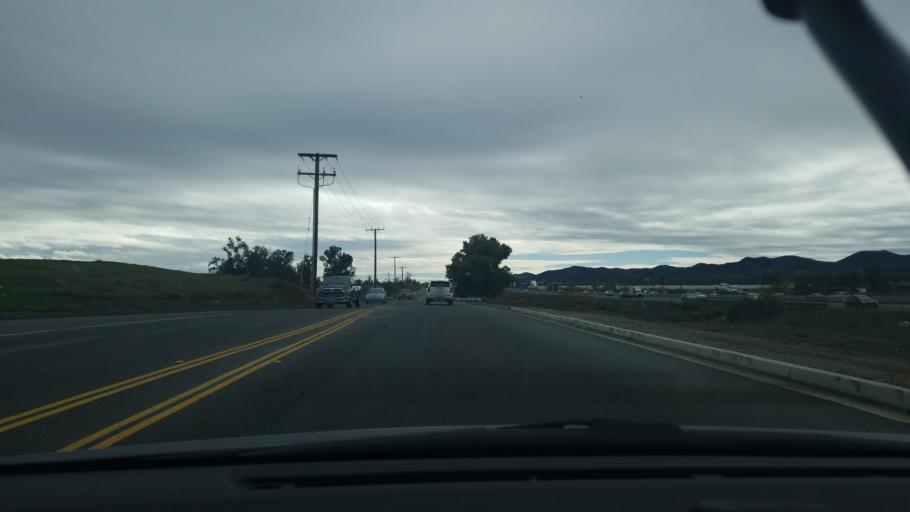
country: US
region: California
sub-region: Riverside County
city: Sun City
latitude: 33.6600
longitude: -117.1705
